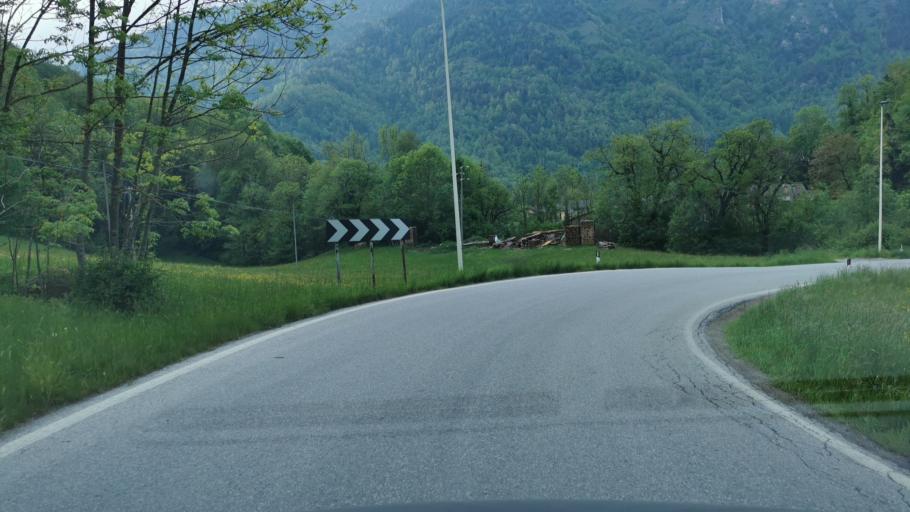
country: IT
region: Piedmont
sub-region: Provincia di Cuneo
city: Monterosso Grana
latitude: 44.4054
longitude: 7.3109
